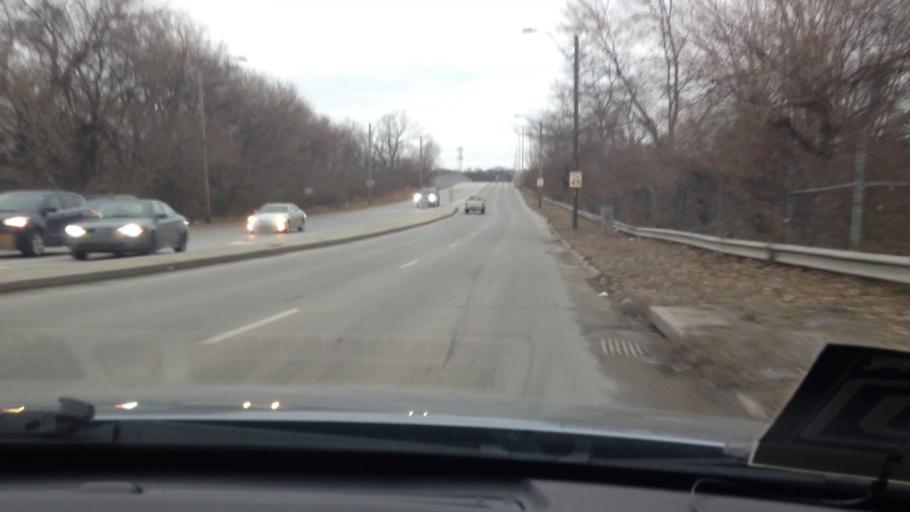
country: US
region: Missouri
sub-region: Clay County
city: North Kansas City
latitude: 39.1269
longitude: -94.5196
